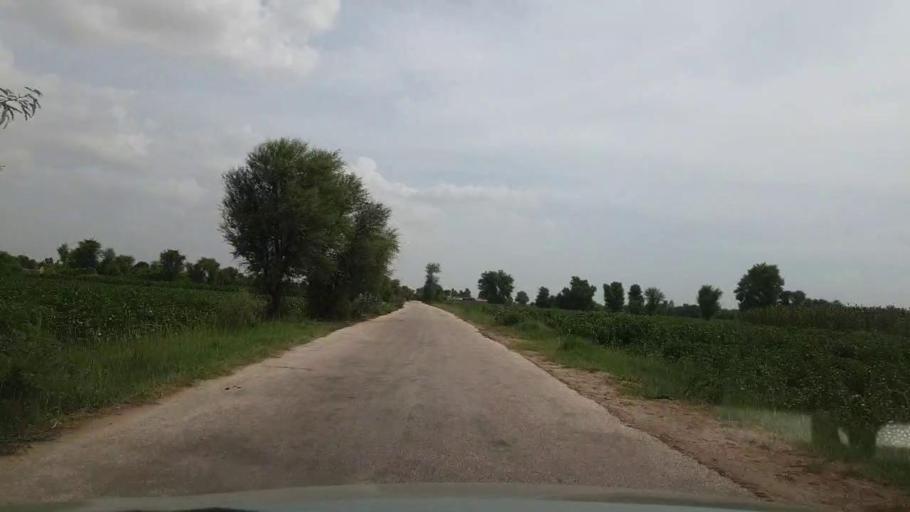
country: PK
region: Sindh
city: Kot Diji
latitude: 27.1408
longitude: 69.0281
